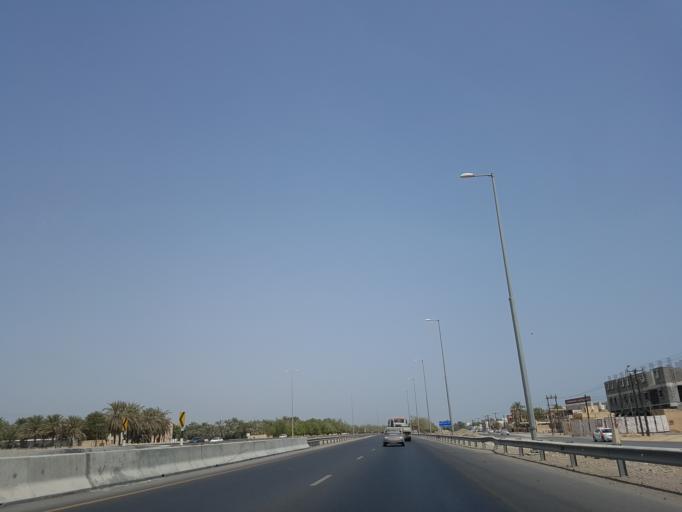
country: OM
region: Al Batinah
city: Saham
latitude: 24.1553
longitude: 56.8671
